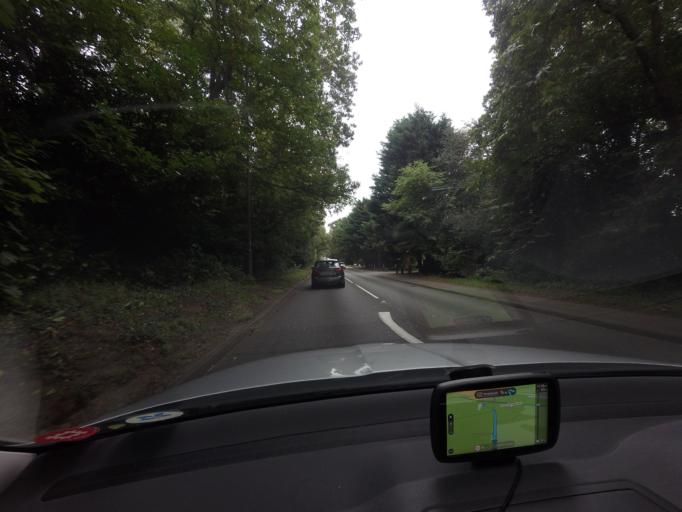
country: GB
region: England
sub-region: Surrey
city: Cobham
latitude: 51.3368
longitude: -0.4412
